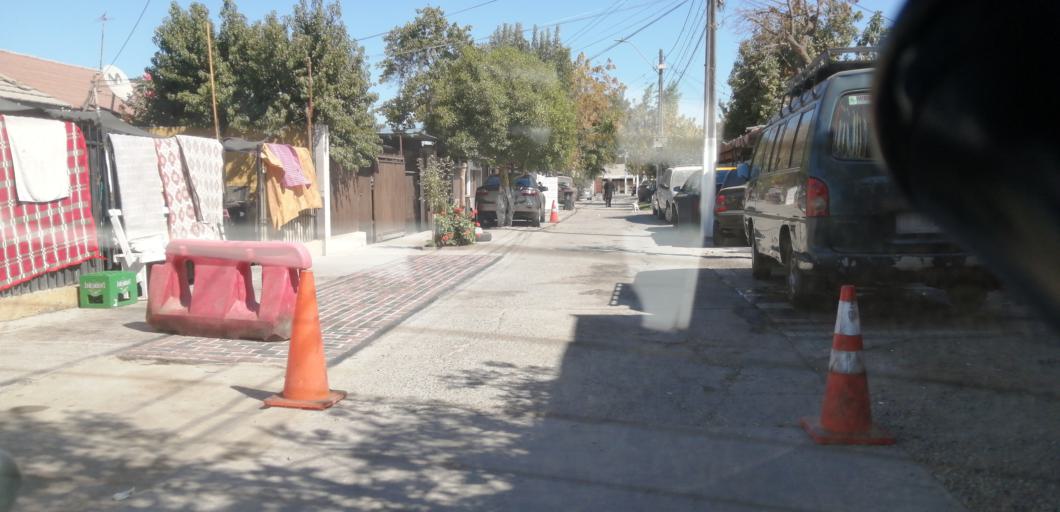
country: CL
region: Santiago Metropolitan
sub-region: Provincia de Santiago
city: Lo Prado
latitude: -33.4347
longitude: -70.7589
